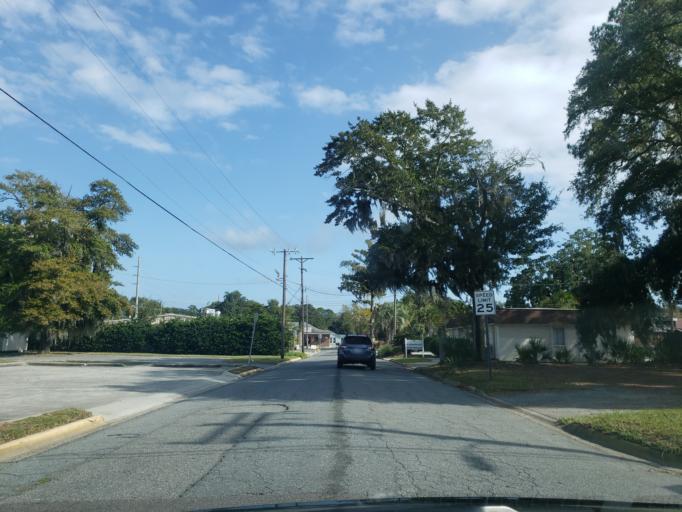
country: US
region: Georgia
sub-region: Chatham County
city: Thunderbolt
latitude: 32.0287
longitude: -81.0942
